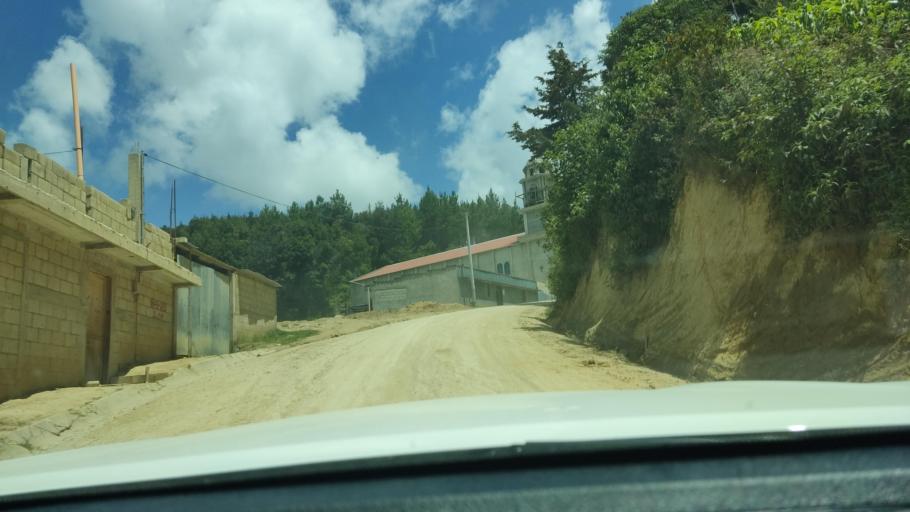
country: GT
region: Chimaltenango
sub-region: Municipio de San Juan Comalapa
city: Comalapa
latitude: 14.7771
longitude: -90.8765
